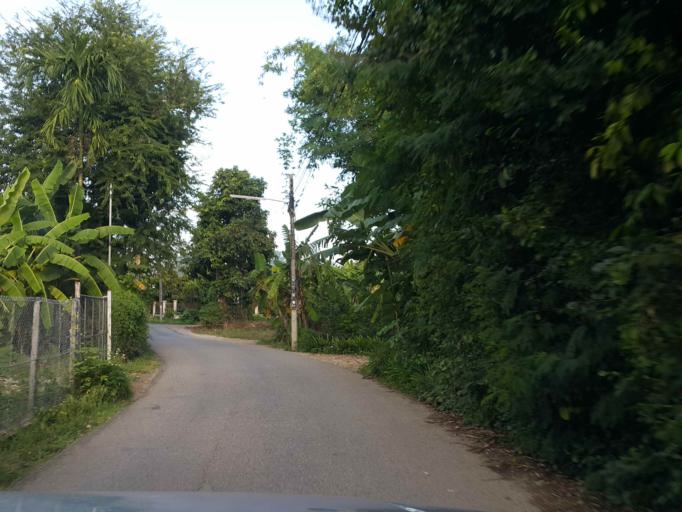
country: TH
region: Chiang Mai
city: San Sai
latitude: 18.8973
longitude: 98.9881
